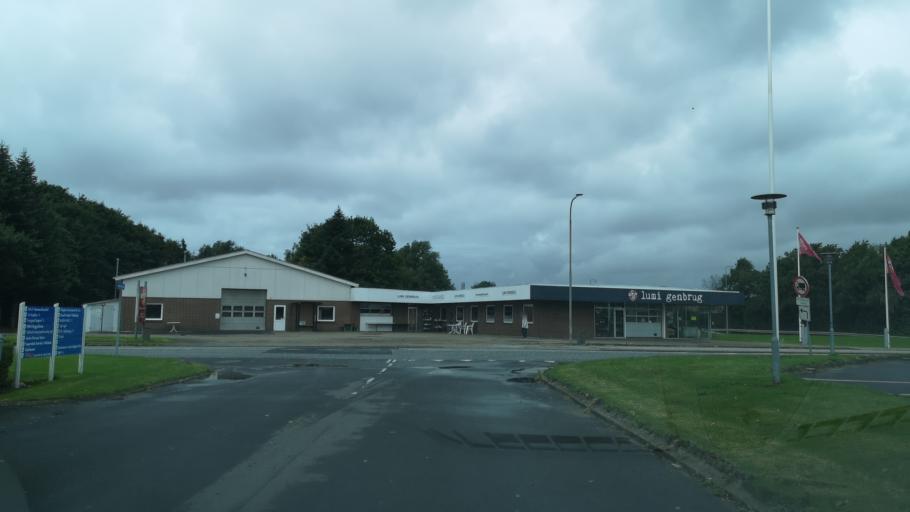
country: DK
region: Central Jutland
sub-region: Ringkobing-Skjern Kommune
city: Videbaek
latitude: 56.0908
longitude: 8.6394
